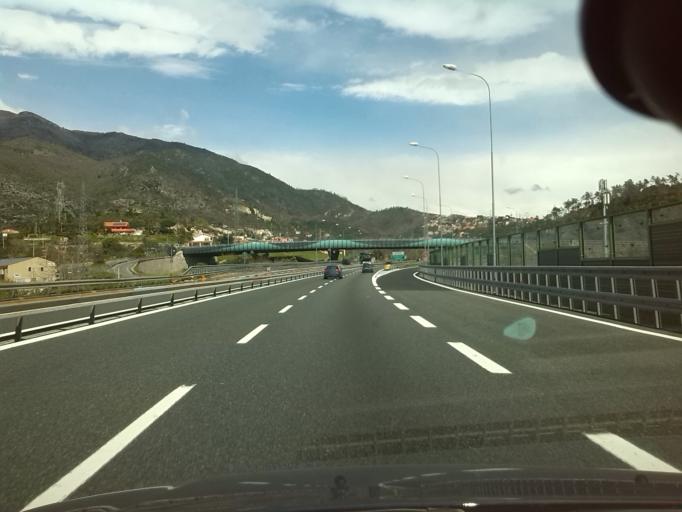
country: IT
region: Liguria
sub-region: Provincia di Savona
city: Boissano
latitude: 44.1216
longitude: 8.2251
